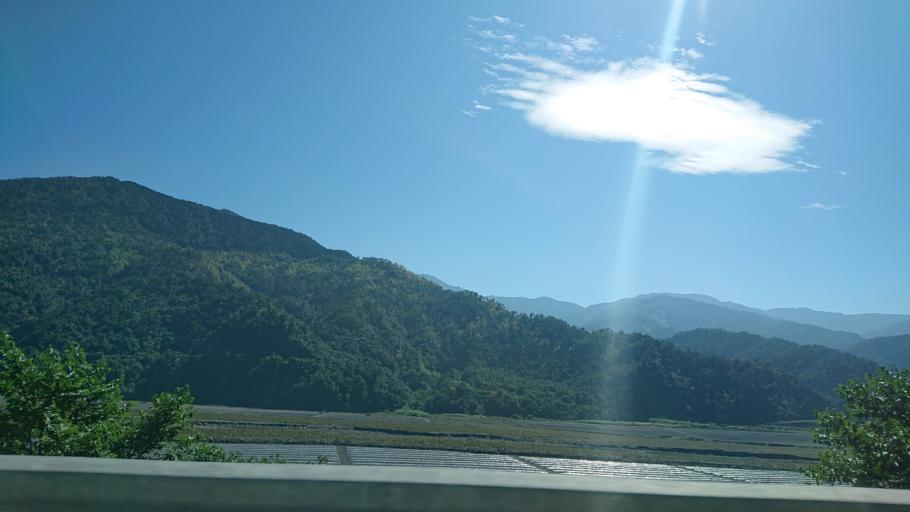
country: TW
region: Taiwan
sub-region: Yilan
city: Yilan
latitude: 24.5859
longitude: 121.5004
